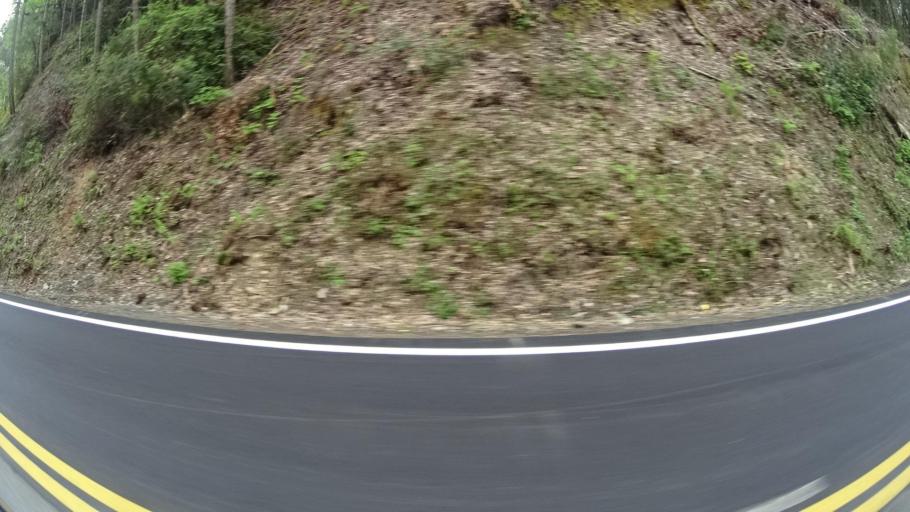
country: US
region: California
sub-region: Humboldt County
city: Willow Creek
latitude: 41.0013
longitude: -123.6285
